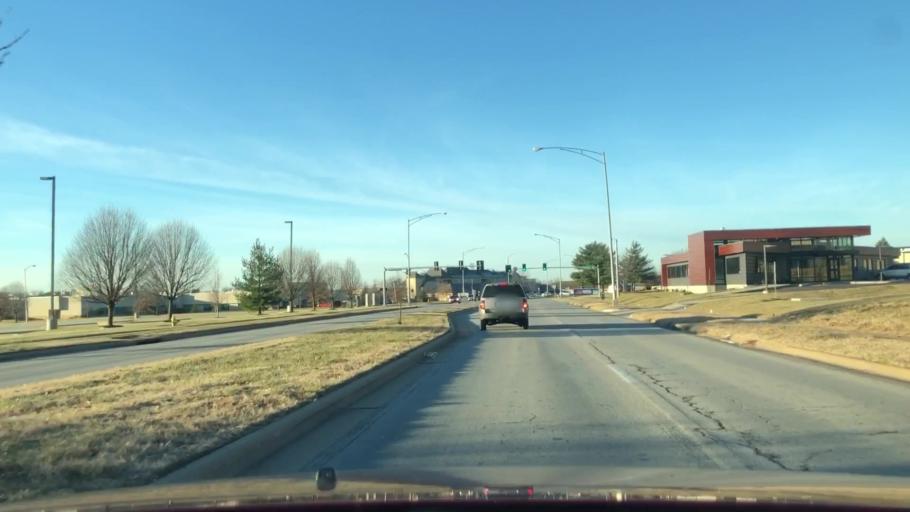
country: US
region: Missouri
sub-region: Greene County
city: Springfield
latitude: 37.1484
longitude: -93.2648
